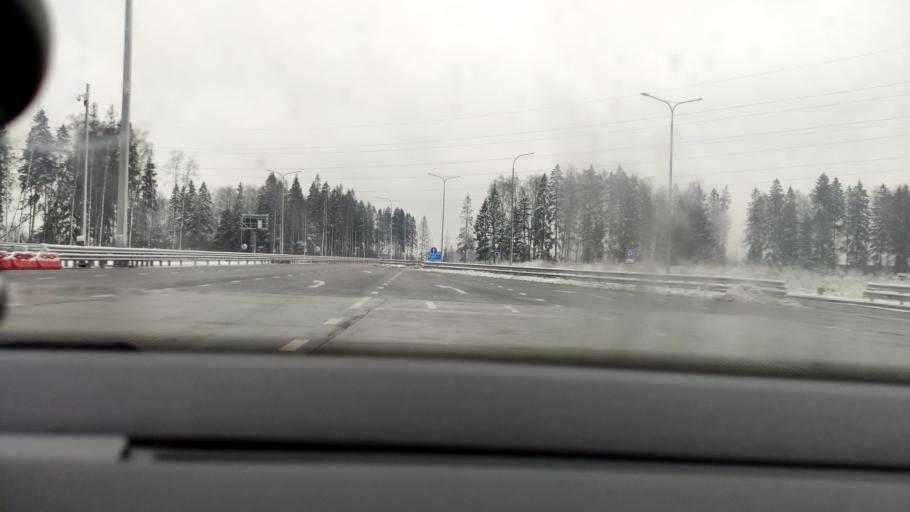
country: RU
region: Moskovskaya
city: Solnechnogorsk
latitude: 56.1617
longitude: 36.9155
